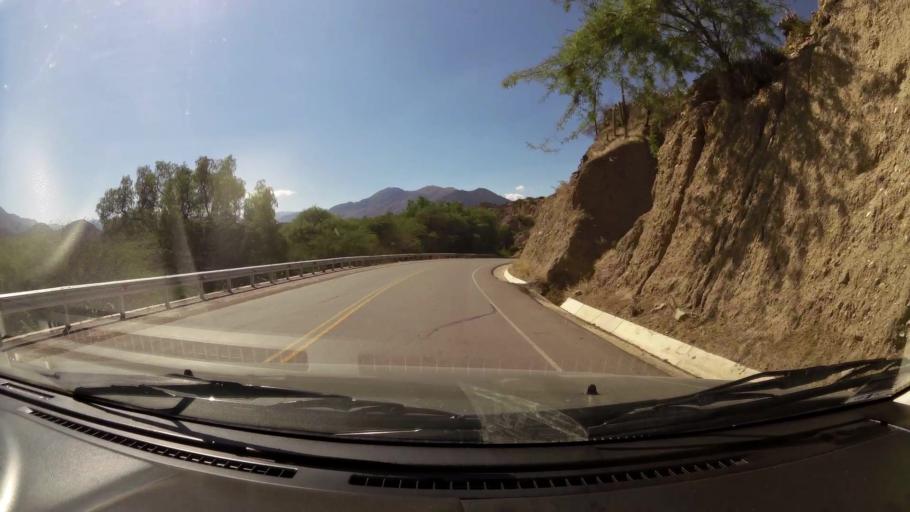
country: PE
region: Ayacucho
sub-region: Provincia de Huanta
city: Luricocha
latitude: -12.8867
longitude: -74.3166
